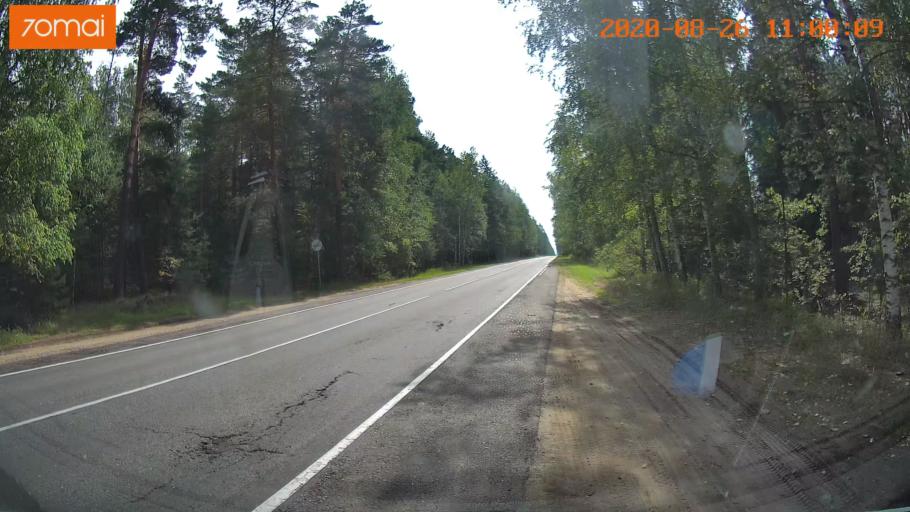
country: RU
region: Rjazan
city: Izhevskoye
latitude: 54.5765
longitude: 41.2115
